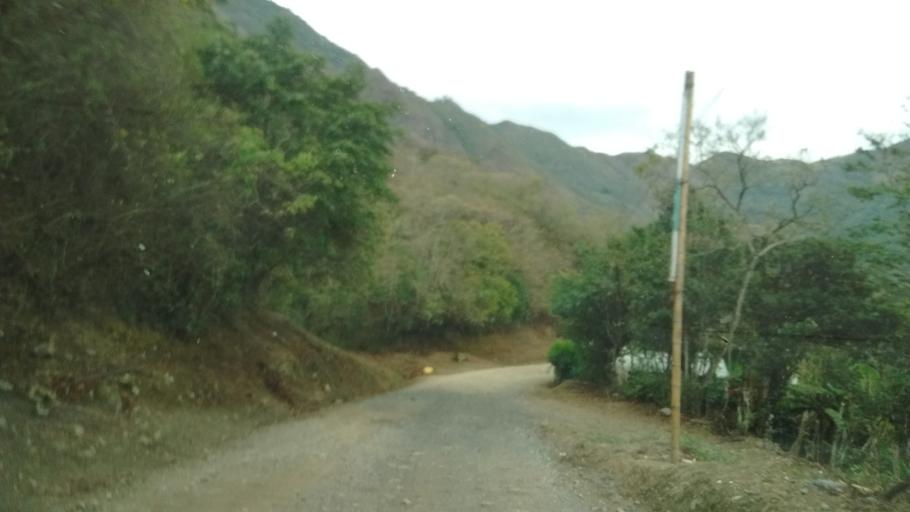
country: CO
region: Cauca
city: Almaguer
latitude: 1.8453
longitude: -76.9047
